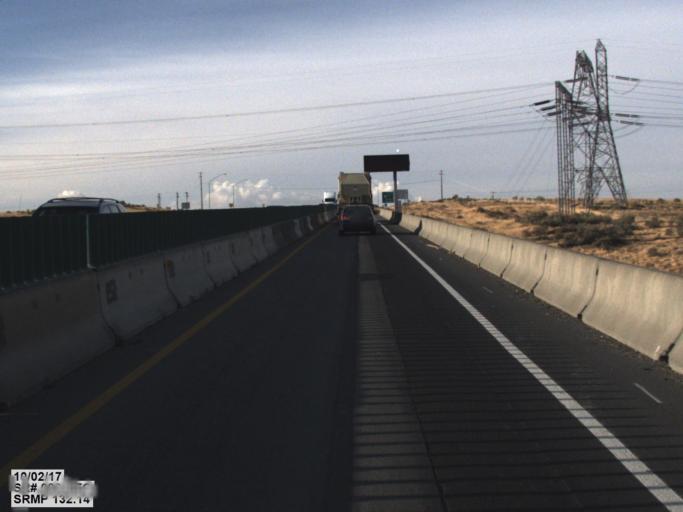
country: US
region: Oregon
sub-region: Umatilla County
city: Umatilla
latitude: 45.9379
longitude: -119.3314
